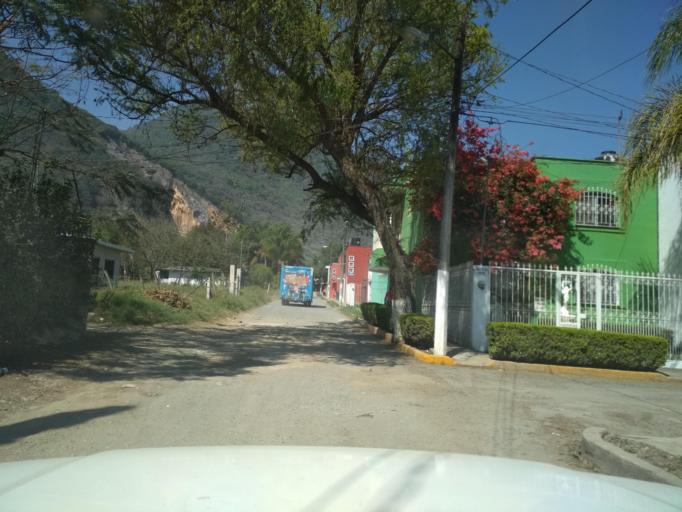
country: MX
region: Veracruz
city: Jalapilla
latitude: 18.8188
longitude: -97.0882
